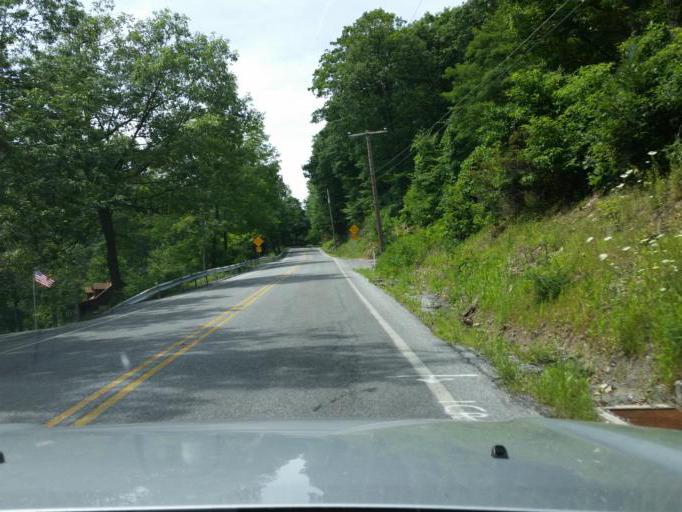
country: US
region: Pennsylvania
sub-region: Blair County
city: Altoona
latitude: 40.5558
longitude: -78.4470
